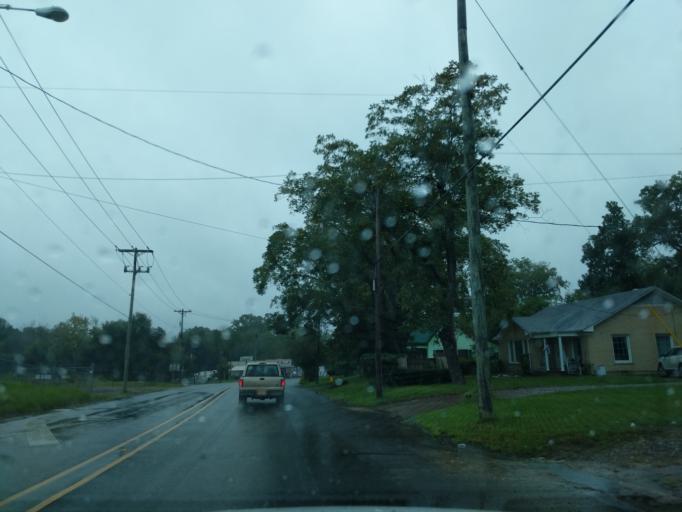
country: US
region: Texas
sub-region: Panola County
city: Carthage
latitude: 32.1577
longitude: -94.3326
